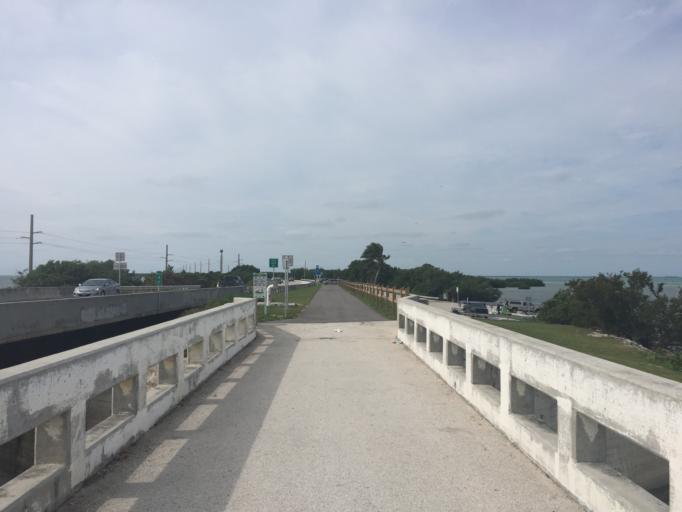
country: US
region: Florida
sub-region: Monroe County
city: Big Pine Key
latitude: 24.6825
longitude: -81.2282
